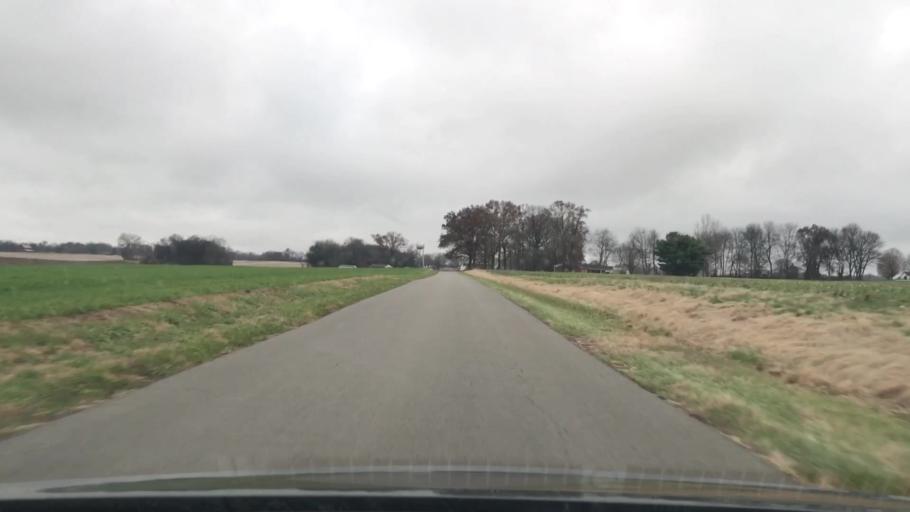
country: US
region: Kentucky
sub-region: Todd County
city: Elkton
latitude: 36.7876
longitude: -87.1512
